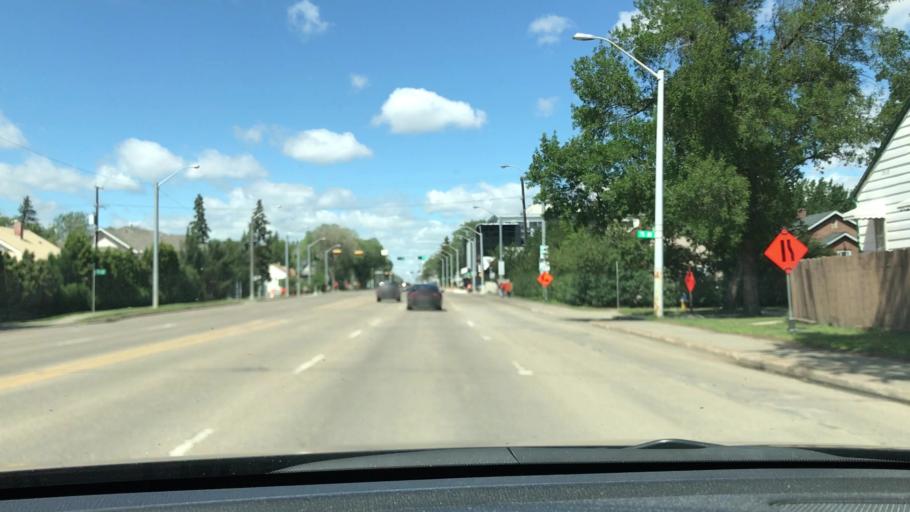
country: CA
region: Alberta
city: Edmonton
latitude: 53.5110
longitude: -113.5118
